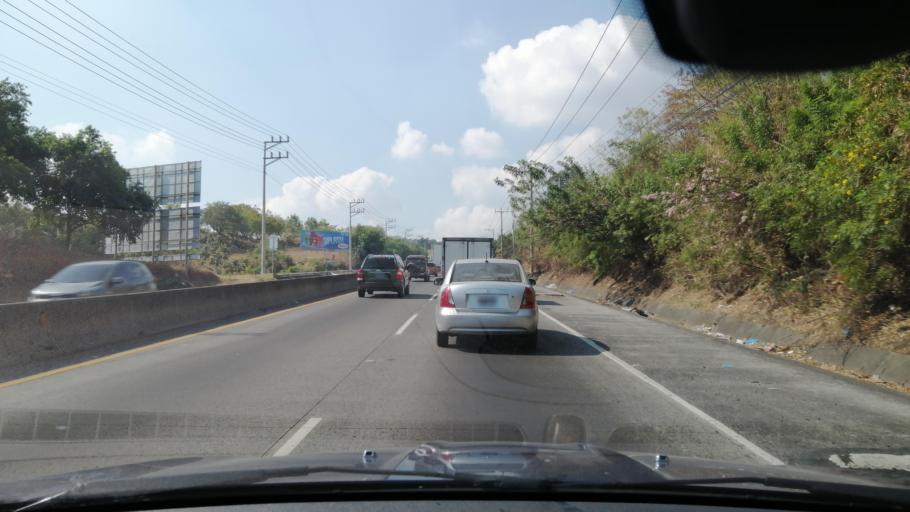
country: SV
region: San Salvador
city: Ayutuxtepeque
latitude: 13.7528
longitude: -89.2172
